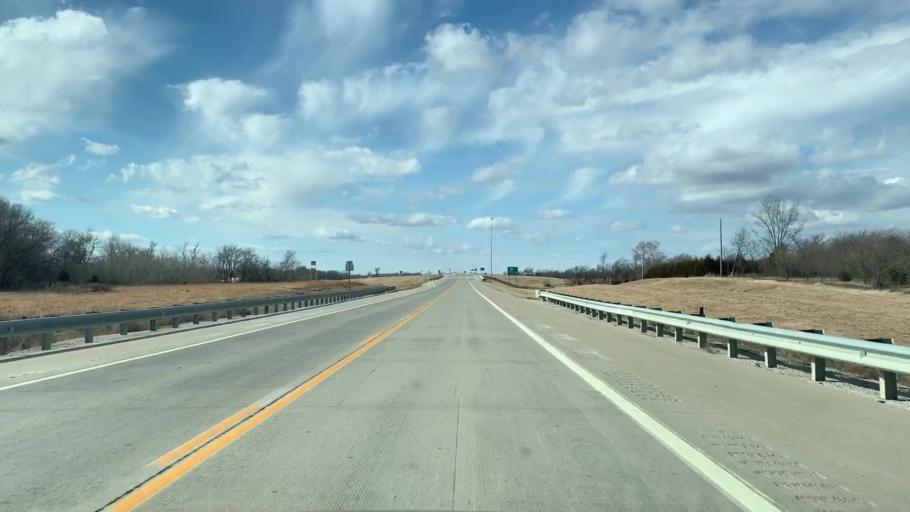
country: US
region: Kansas
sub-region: Labette County
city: Parsons
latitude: 37.3653
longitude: -95.2493
